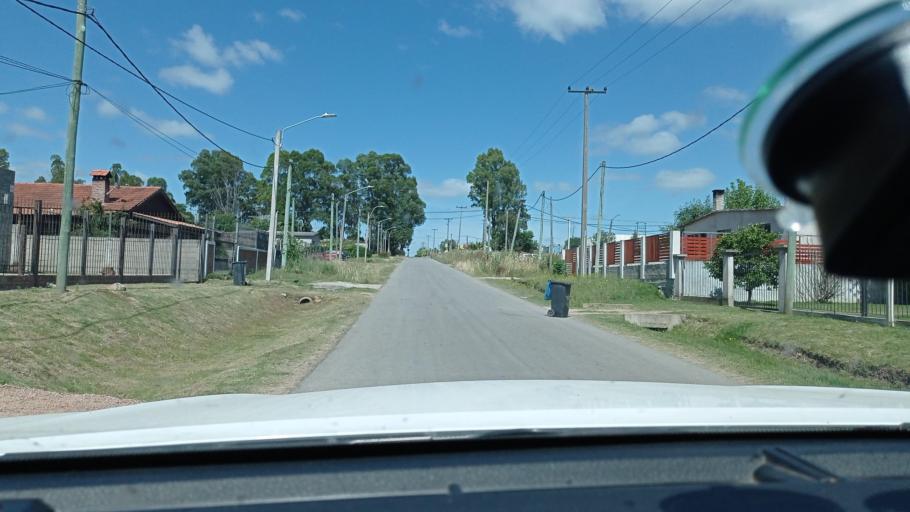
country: UY
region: Canelones
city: Pando
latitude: -34.7152
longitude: -55.9651
